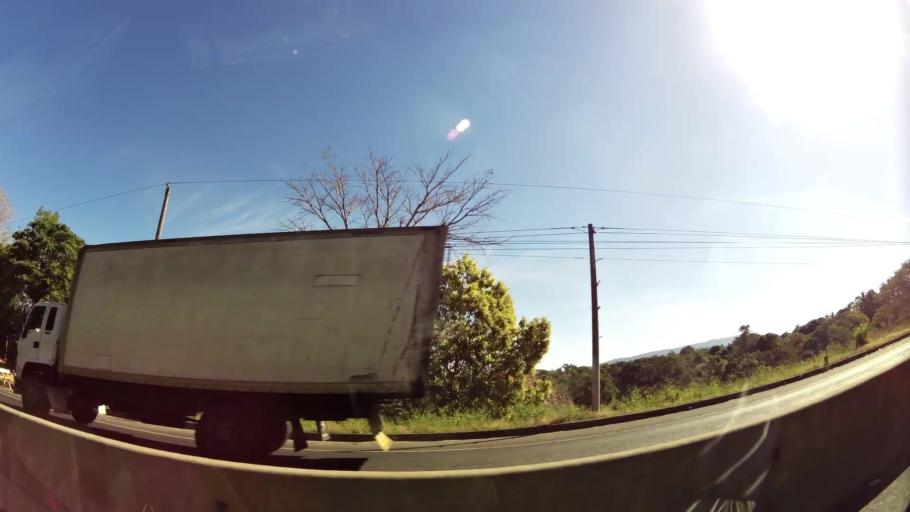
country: SV
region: Santa Ana
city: Coatepeque
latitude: 13.9233
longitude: -89.5193
